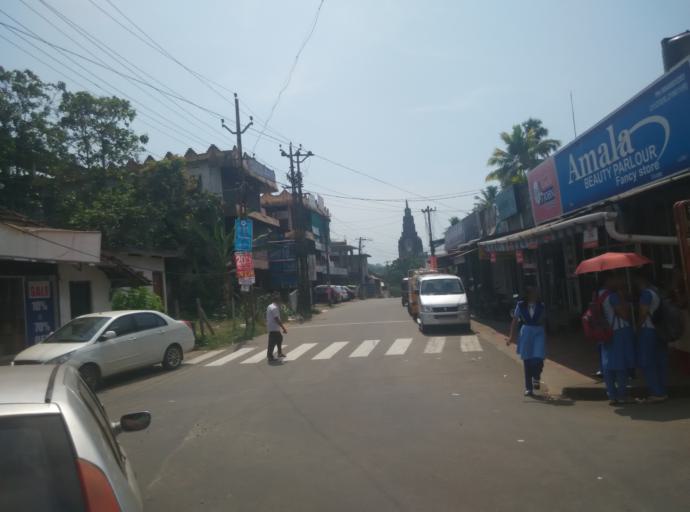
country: IN
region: Kerala
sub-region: Kottayam
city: Lalam
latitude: 9.7148
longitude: 76.6824
